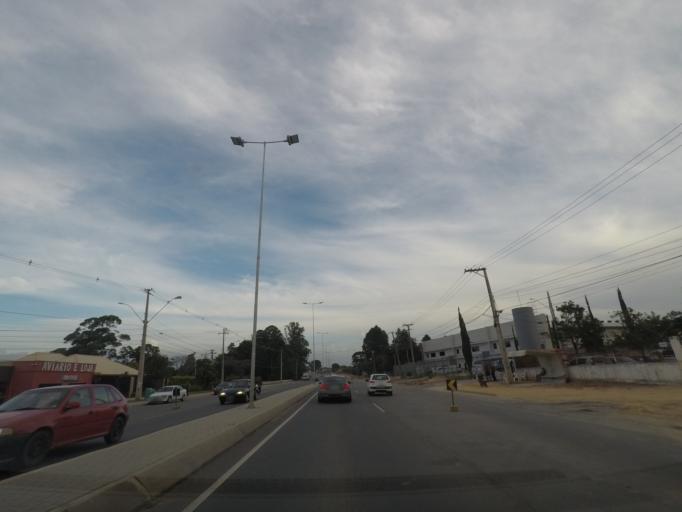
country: BR
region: Parana
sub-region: Colombo
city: Colombo
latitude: -25.3356
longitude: -49.2211
